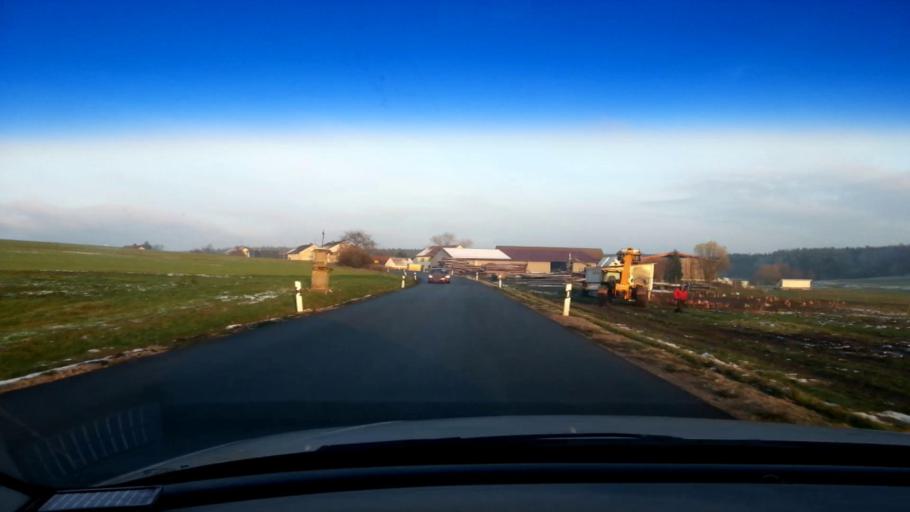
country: DE
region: Bavaria
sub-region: Regierungsbezirk Mittelfranken
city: Gremsdorf
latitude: 49.7343
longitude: 10.8467
